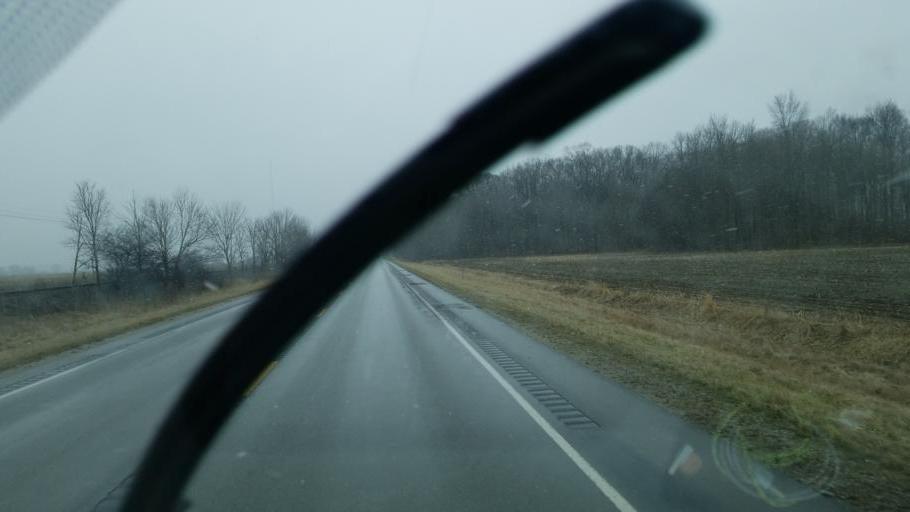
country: US
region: Indiana
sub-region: Wabash County
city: Mount Vernon
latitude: 40.7043
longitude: -85.7590
